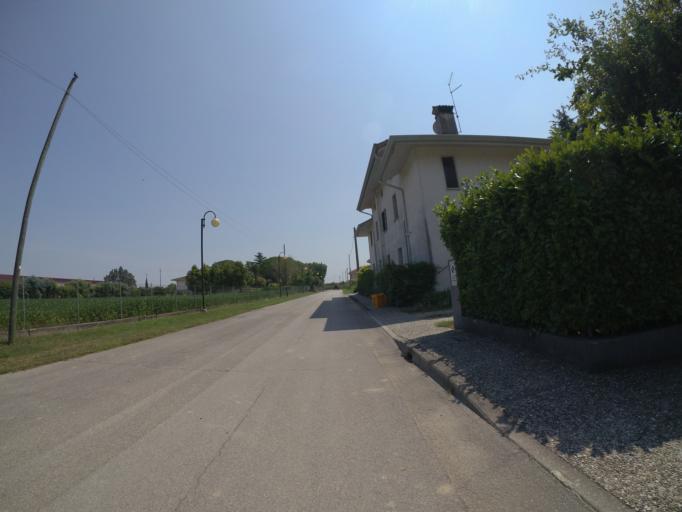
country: IT
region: Friuli Venezia Giulia
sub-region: Provincia di Udine
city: Varmo
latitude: 45.9040
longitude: 12.9993
